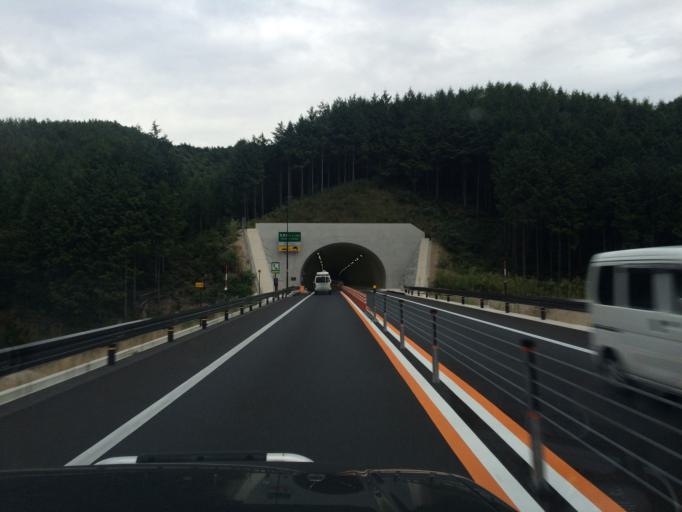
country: JP
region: Tottori
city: Tottori
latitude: 35.4999
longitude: 134.0626
